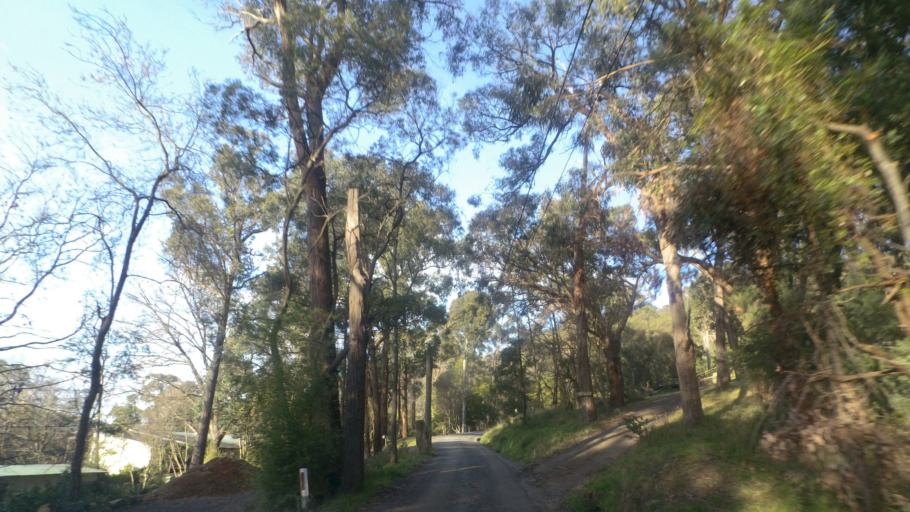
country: AU
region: Victoria
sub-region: Yarra Ranges
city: Montrose
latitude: -37.8164
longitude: 145.3551
